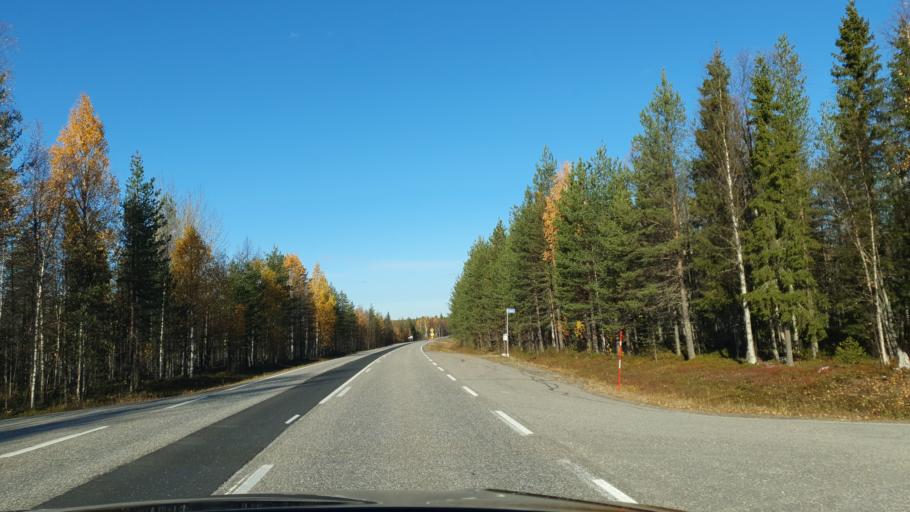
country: FI
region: Lapland
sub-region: Tunturi-Lappi
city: Kittilae
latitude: 67.2552
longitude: 24.8990
